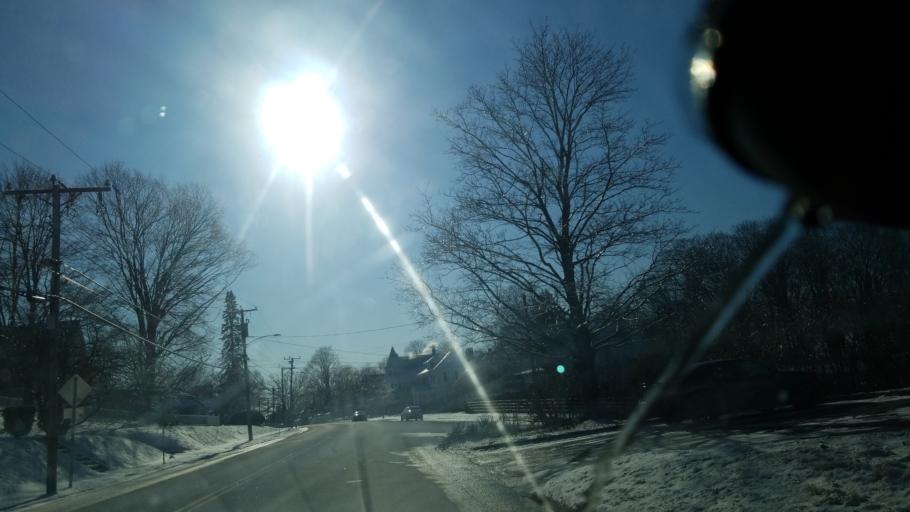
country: US
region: Connecticut
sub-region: Windham County
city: Danielson
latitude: 41.8035
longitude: -71.8800
